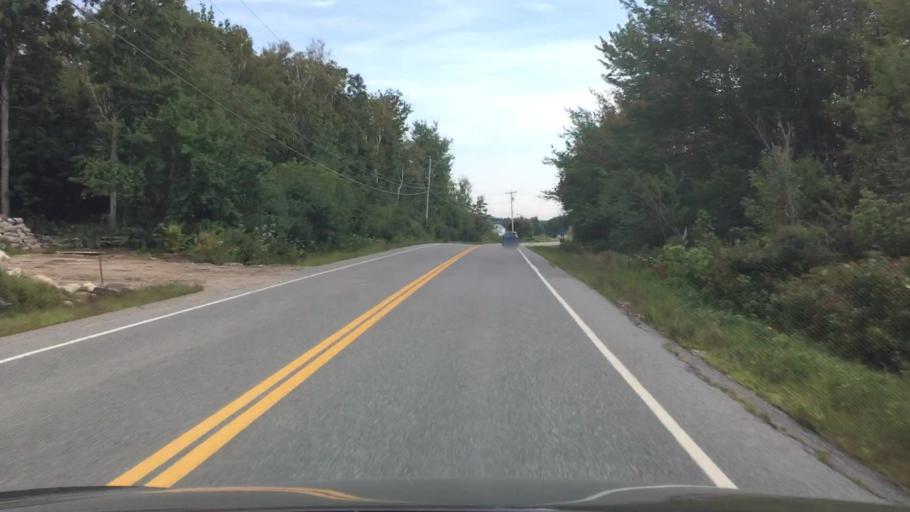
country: US
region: Maine
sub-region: Hancock County
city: Penobscot
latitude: 44.4682
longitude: -68.7817
